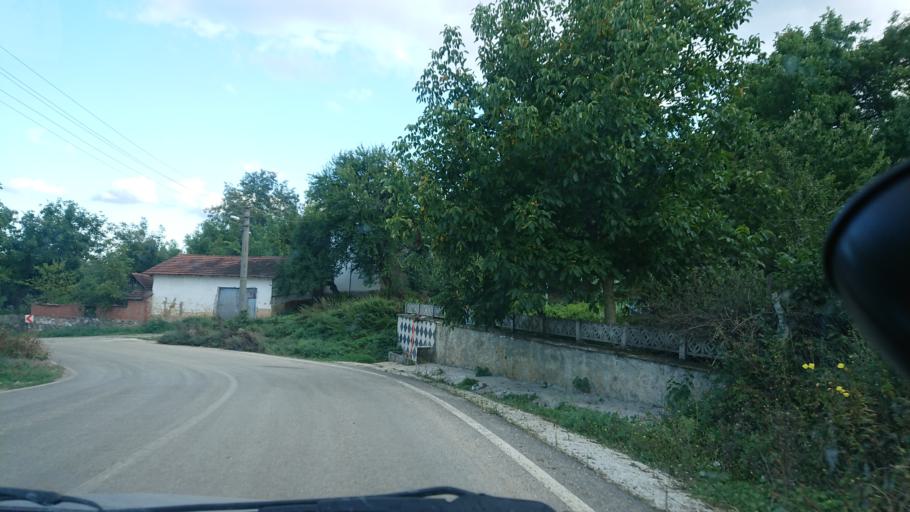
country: TR
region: Bilecik
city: Pazaryeri
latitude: 40.0105
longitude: 29.7986
